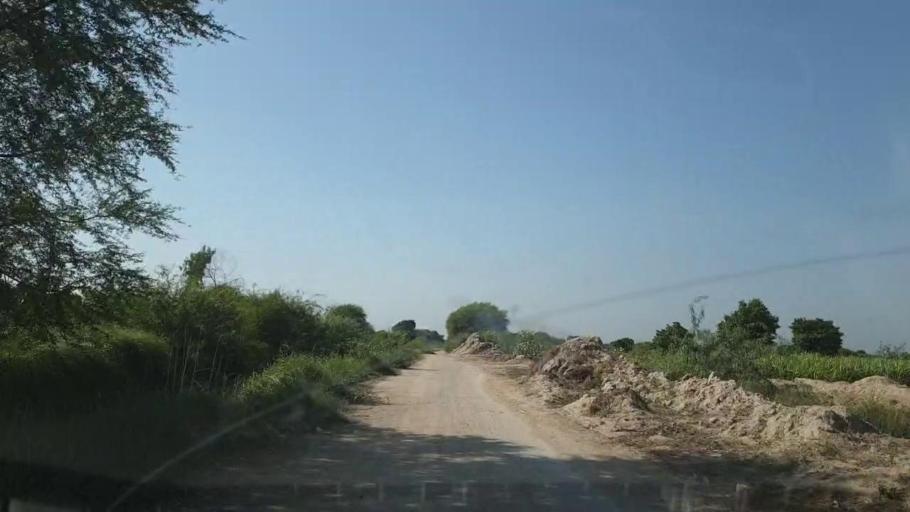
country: PK
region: Sindh
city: Tando Jam
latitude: 25.3092
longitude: 68.6137
